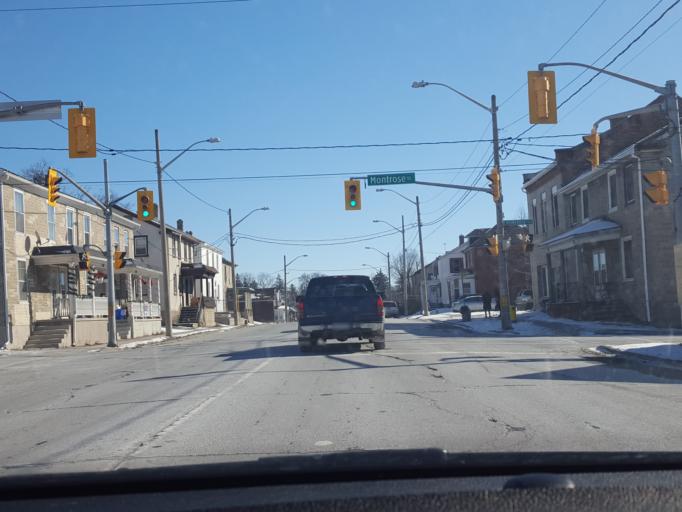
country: CA
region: Ontario
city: Cambridge
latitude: 43.3915
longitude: -80.3499
